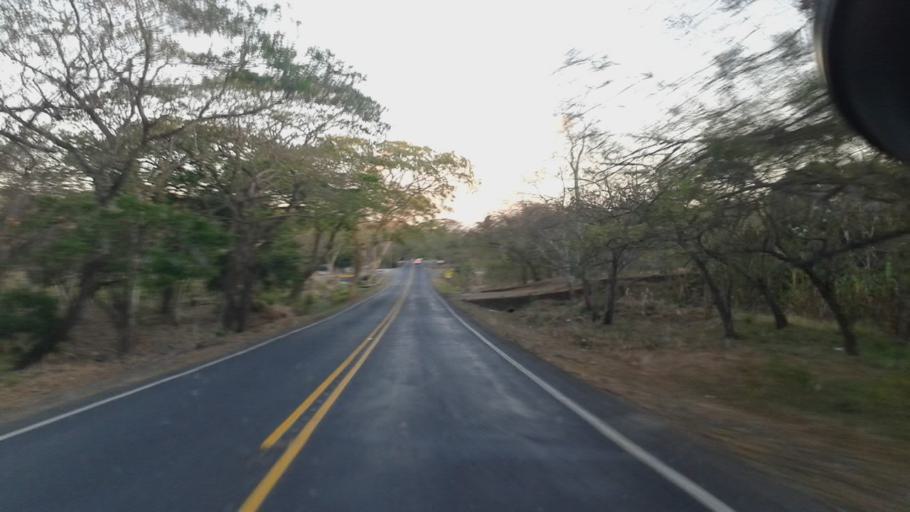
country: CR
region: Guanacaste
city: Juntas
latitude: 10.1375
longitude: -84.9059
